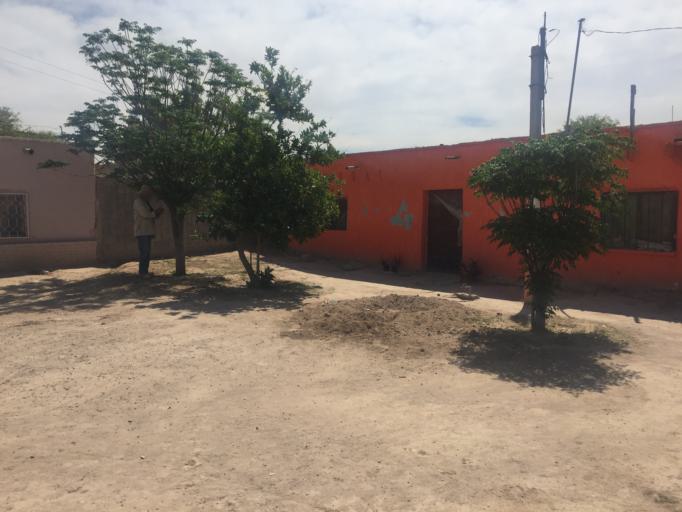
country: MX
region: Durango
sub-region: Gomez Palacio
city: El Vergel
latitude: 25.6717
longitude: -103.5275
